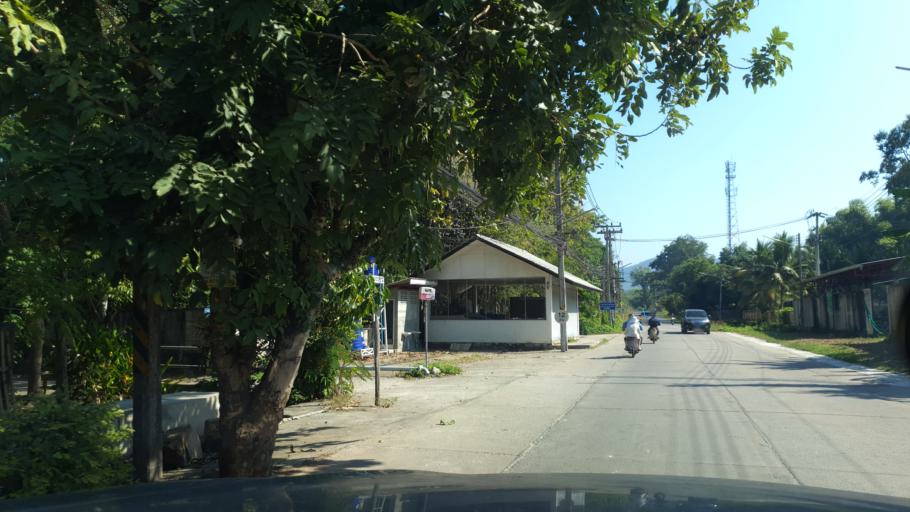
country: TH
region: Chiang Mai
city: San Sai
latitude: 18.8741
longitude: 99.1471
